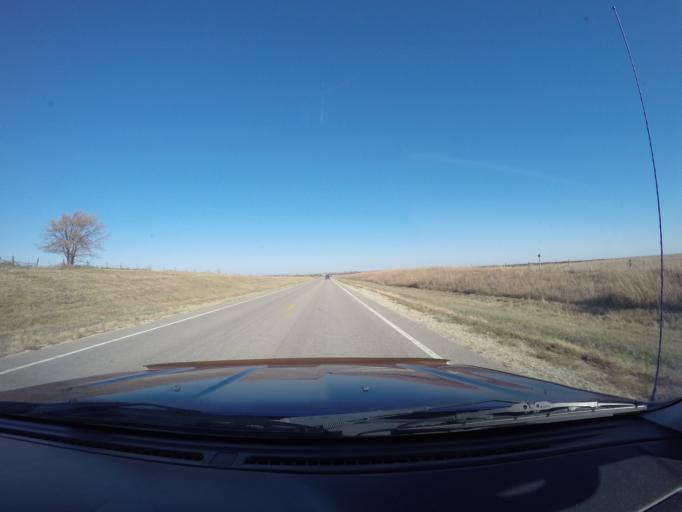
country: US
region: Kansas
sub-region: Riley County
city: Ogden
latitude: 39.3055
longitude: -96.7557
